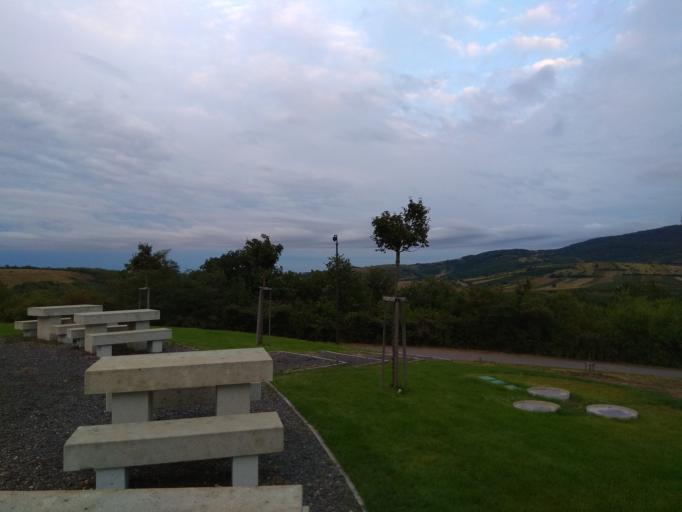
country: HU
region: Borsod-Abauj-Zemplen
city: Tarcal
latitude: 48.1480
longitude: 21.3343
